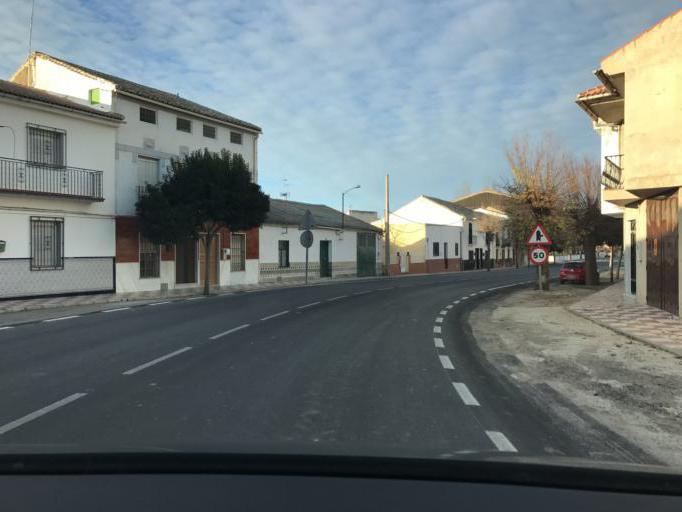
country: ES
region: Andalusia
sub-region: Provincia de Jaen
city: Guadahortuna
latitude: 37.5567
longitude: -3.3980
